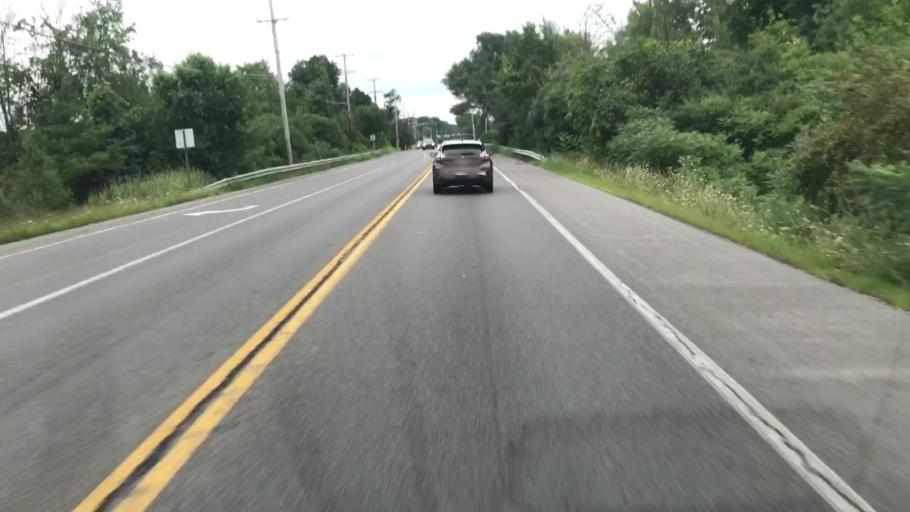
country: US
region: New York
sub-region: Onondaga County
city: North Syracuse
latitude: 43.1395
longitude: -76.1749
